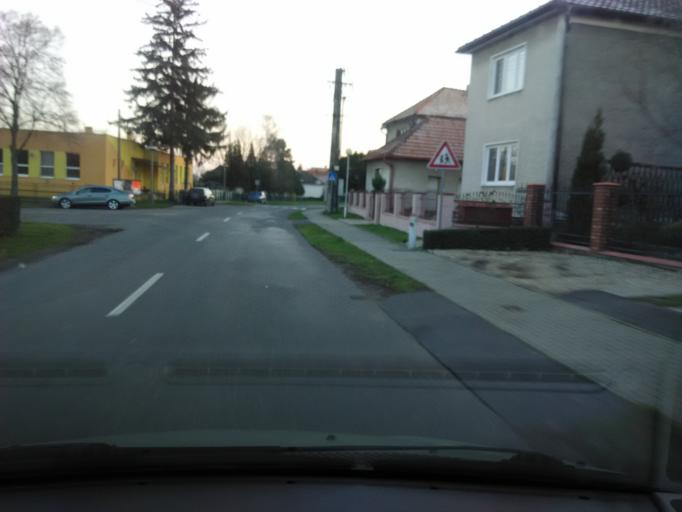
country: SK
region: Nitriansky
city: Tlmace
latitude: 48.2706
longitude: 18.5391
